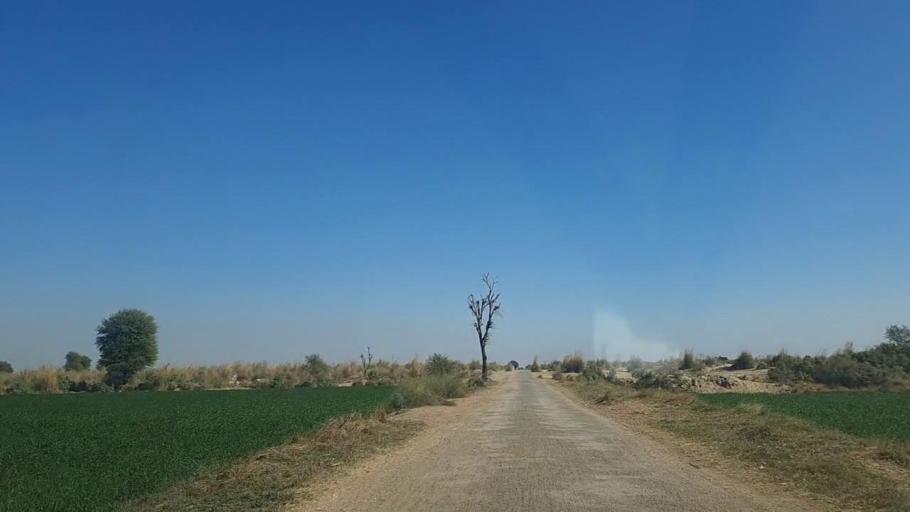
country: PK
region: Sindh
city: Khadro
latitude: 26.2093
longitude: 68.8495
